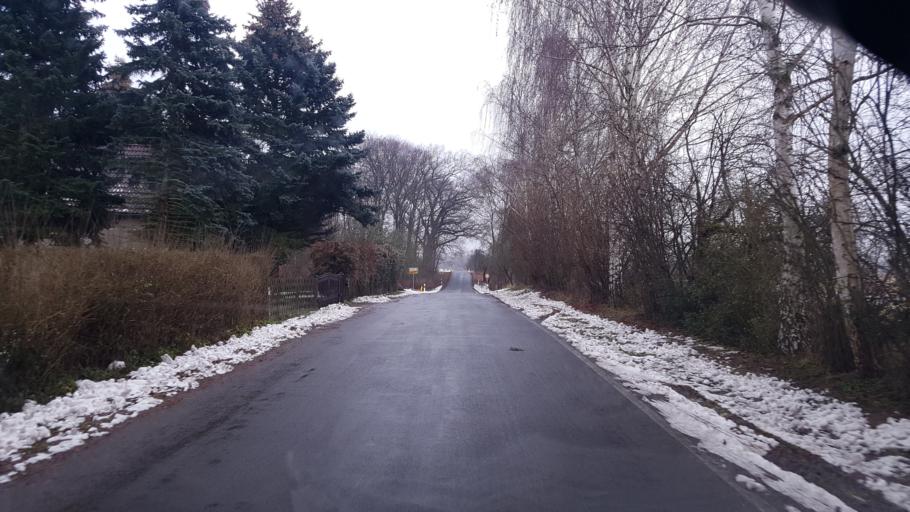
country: DE
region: Brandenburg
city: Lieberose
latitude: 51.9816
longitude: 14.3129
